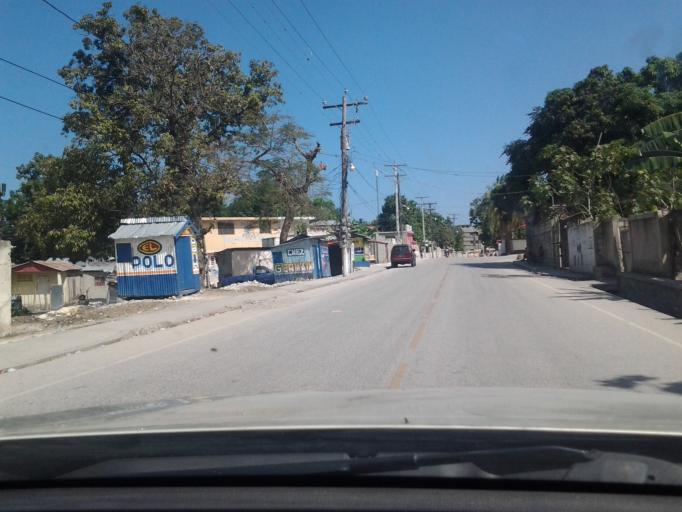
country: HT
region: Ouest
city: Tigwav
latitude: 18.4382
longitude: -72.8548
